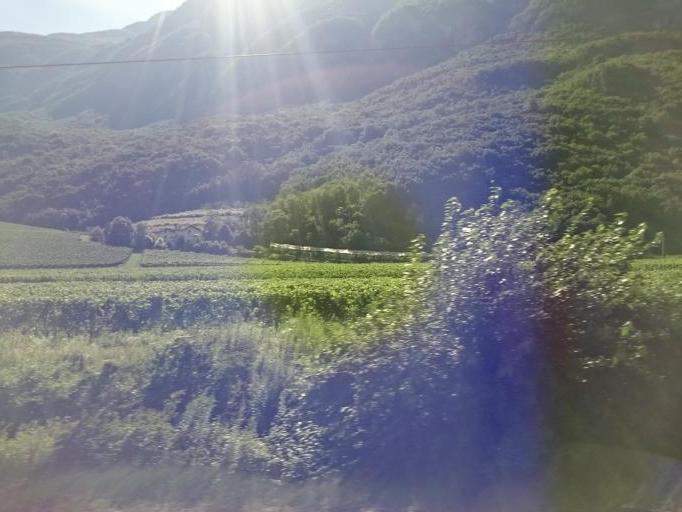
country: IT
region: Trentino-Alto Adige
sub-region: Provincia di Trento
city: Aldeno
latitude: 45.9844
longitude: 11.1169
